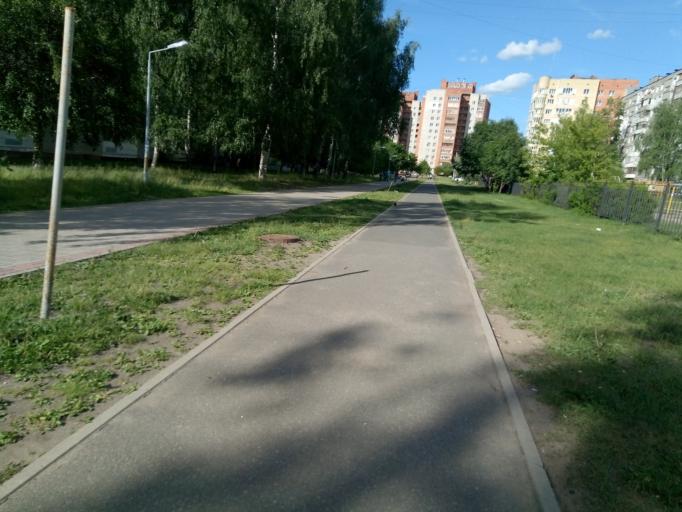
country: RU
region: Jaroslavl
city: Yaroslavl
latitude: 57.6546
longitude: 39.9496
